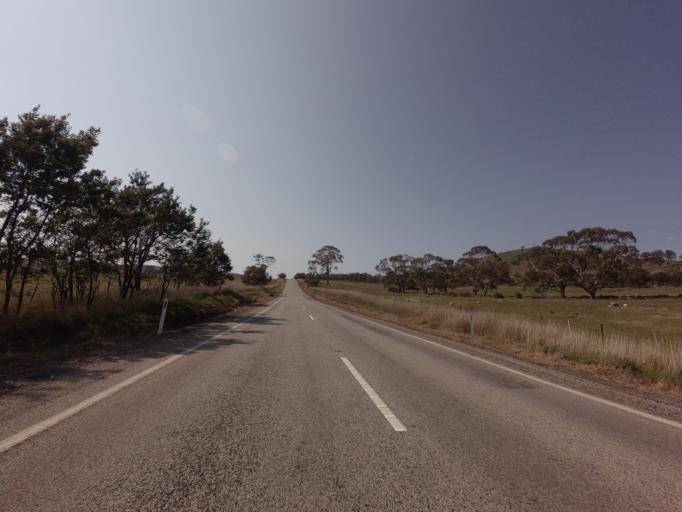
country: AU
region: Tasmania
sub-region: Northern Midlands
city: Evandale
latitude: -41.8205
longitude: 147.5329
